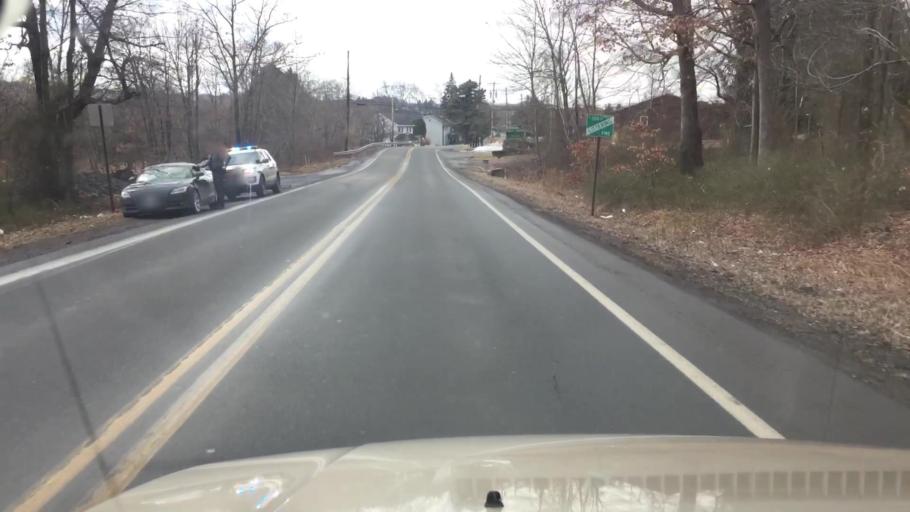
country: US
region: Pennsylvania
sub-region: Luzerne County
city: Harleigh
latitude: 40.9830
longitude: -75.9673
